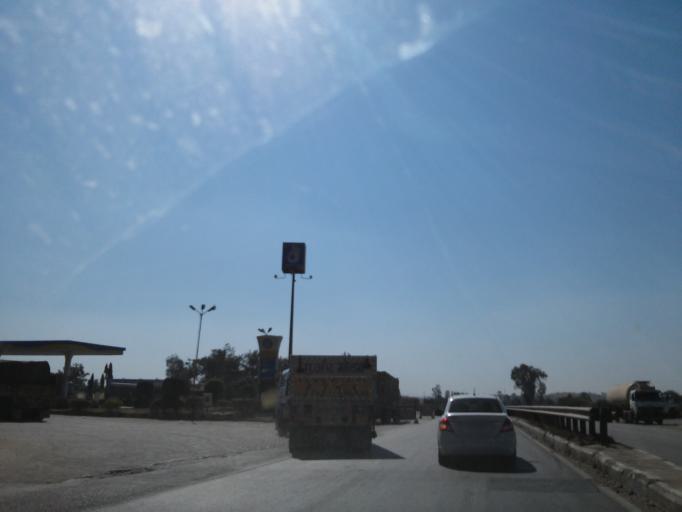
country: IN
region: Rajasthan
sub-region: Dungarpur
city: Dungarpur
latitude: 23.8054
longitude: 73.5227
